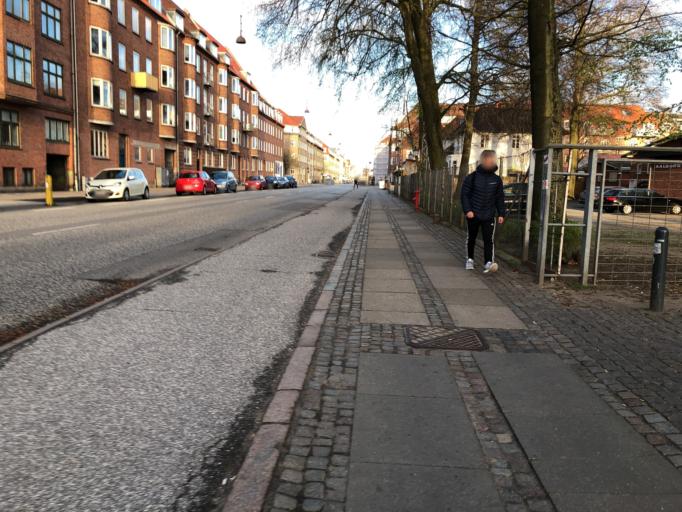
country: DK
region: North Denmark
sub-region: Alborg Kommune
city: Aalborg
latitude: 57.0544
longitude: 9.8998
